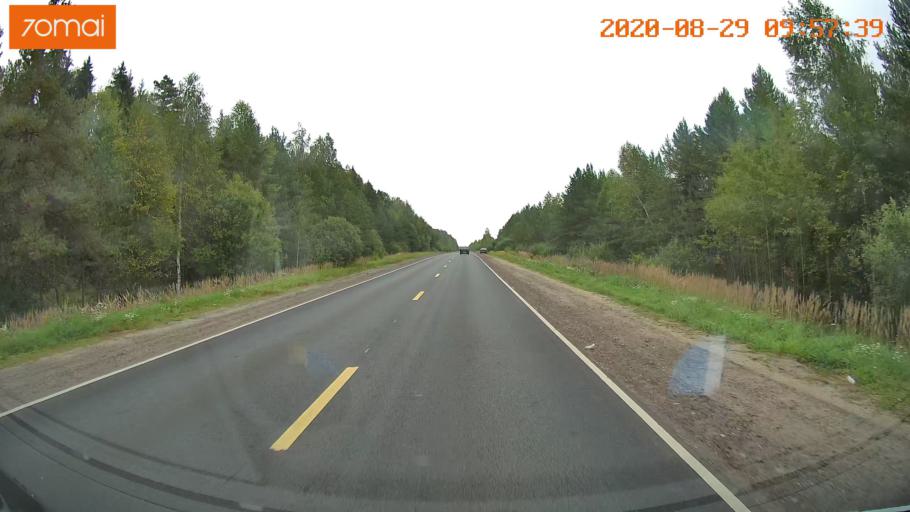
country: RU
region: Ivanovo
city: Zarechnyy
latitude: 57.4158
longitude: 42.3195
